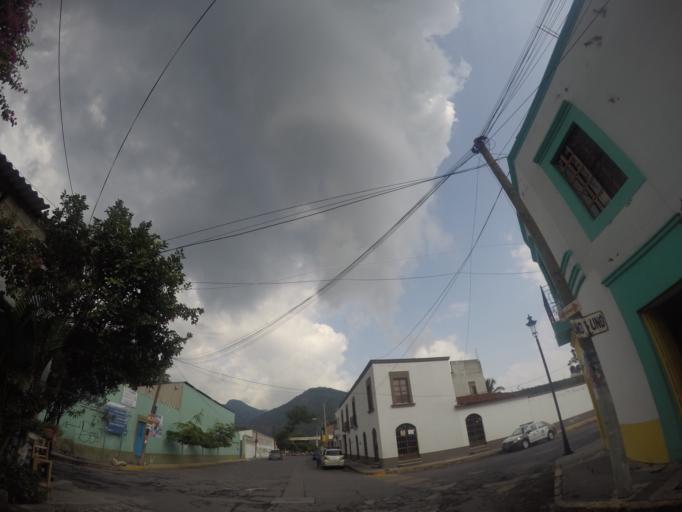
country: MX
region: Nayarit
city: Jala
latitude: 21.1038
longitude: -104.4326
